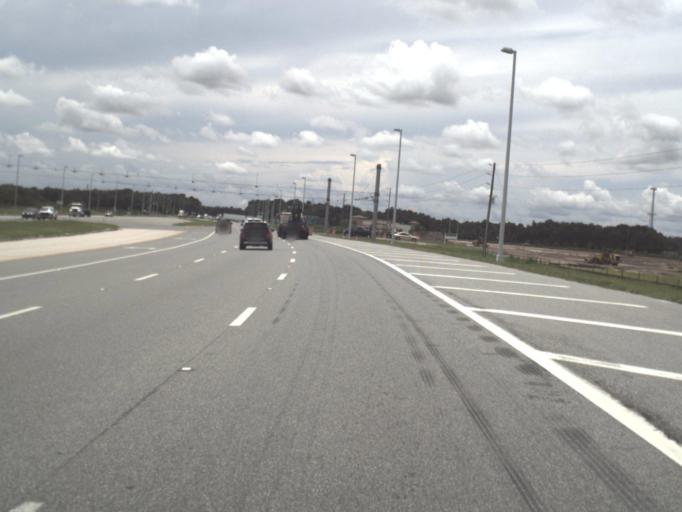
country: US
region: Florida
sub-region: Hillsborough County
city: Pebble Creek
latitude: 28.1940
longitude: -82.3928
